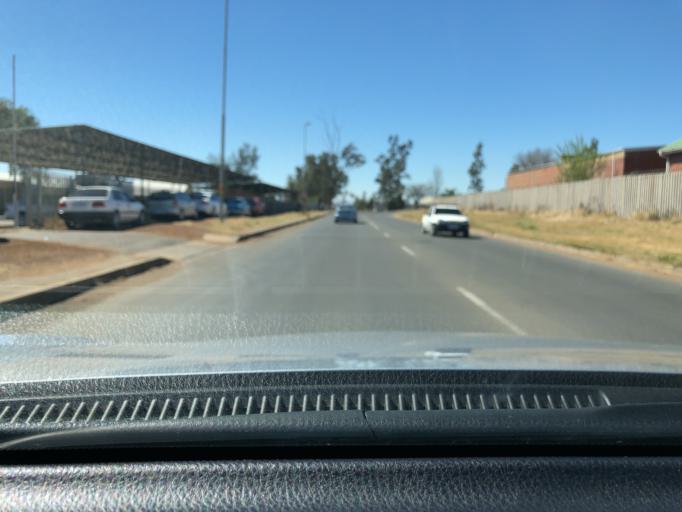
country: ZA
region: KwaZulu-Natal
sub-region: Amajuba District Municipality
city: Newcastle
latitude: -27.7602
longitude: 29.9508
